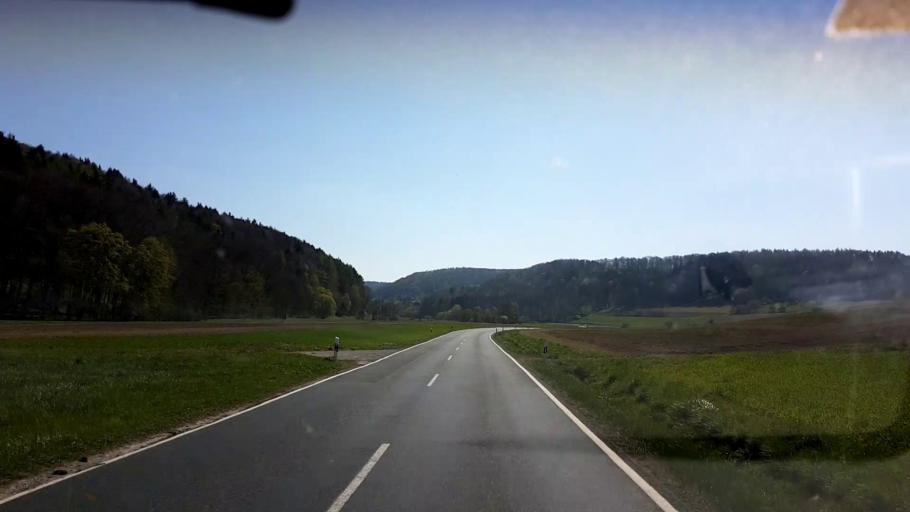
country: DE
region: Bavaria
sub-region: Upper Franconia
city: Unterleinleiter
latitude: 49.8366
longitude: 11.1921
